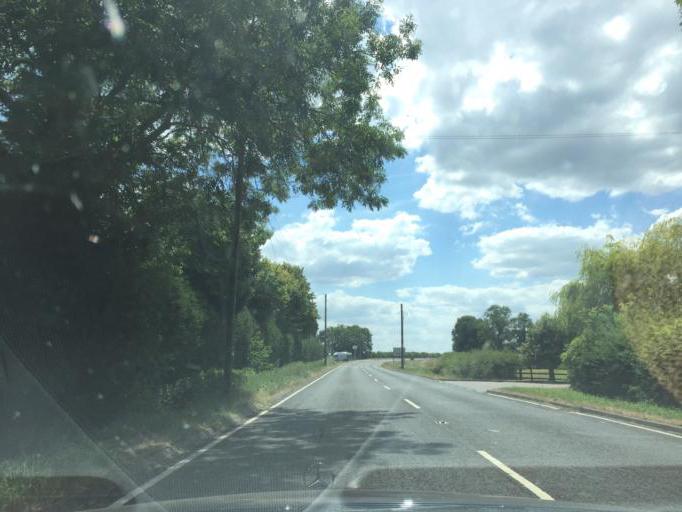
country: GB
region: England
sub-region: Leicestershire
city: Hinckley
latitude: 52.4744
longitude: -1.3767
